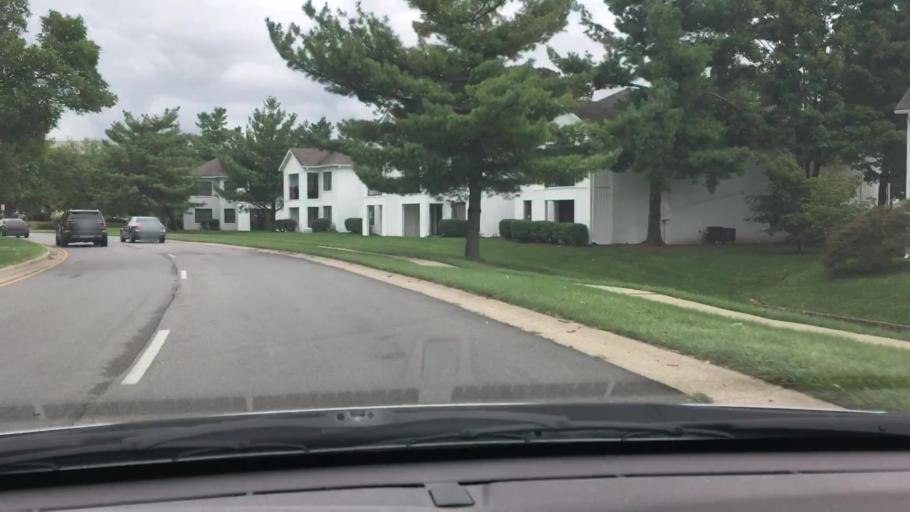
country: US
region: Kentucky
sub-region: Jefferson County
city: Beechwood Village
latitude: 38.2409
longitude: -85.6326
